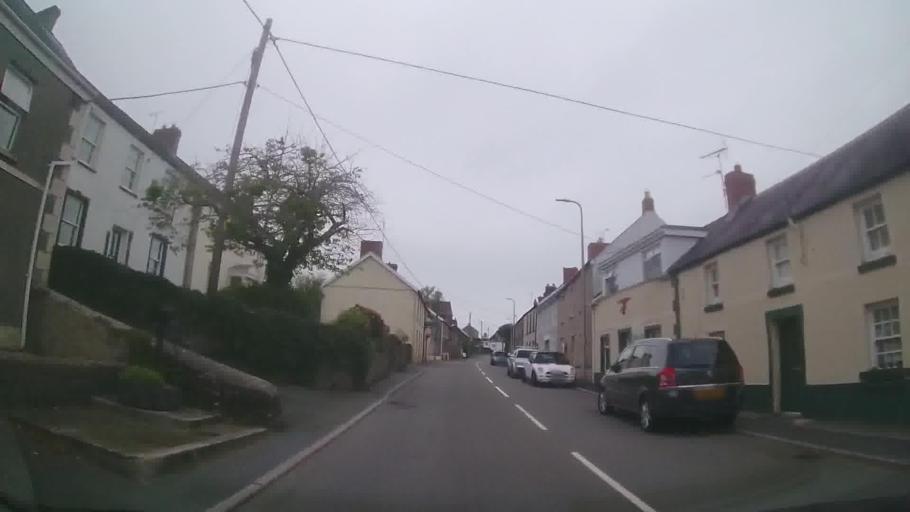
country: GB
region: Wales
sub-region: Carmarthenshire
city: Saint Clears
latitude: 51.8139
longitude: -4.4962
